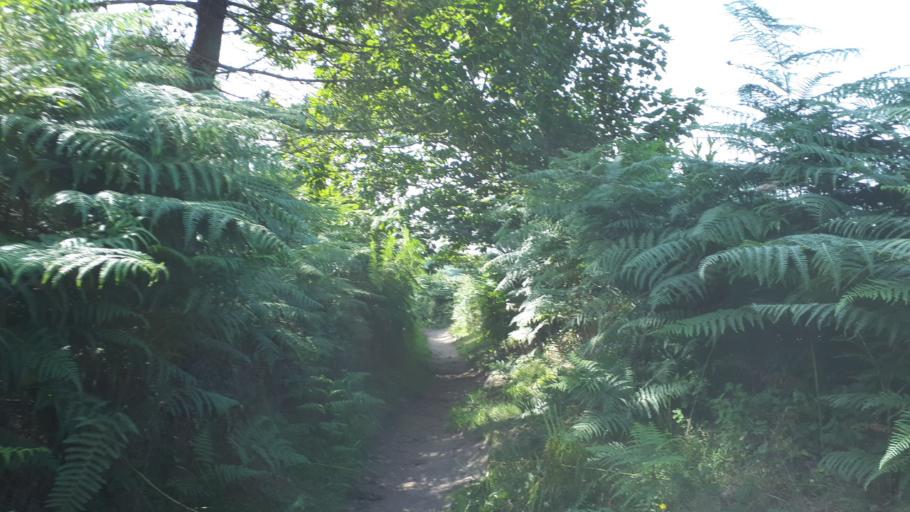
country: FR
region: Brittany
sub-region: Departement du Finistere
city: Carantec
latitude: 48.6713
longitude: -3.8942
